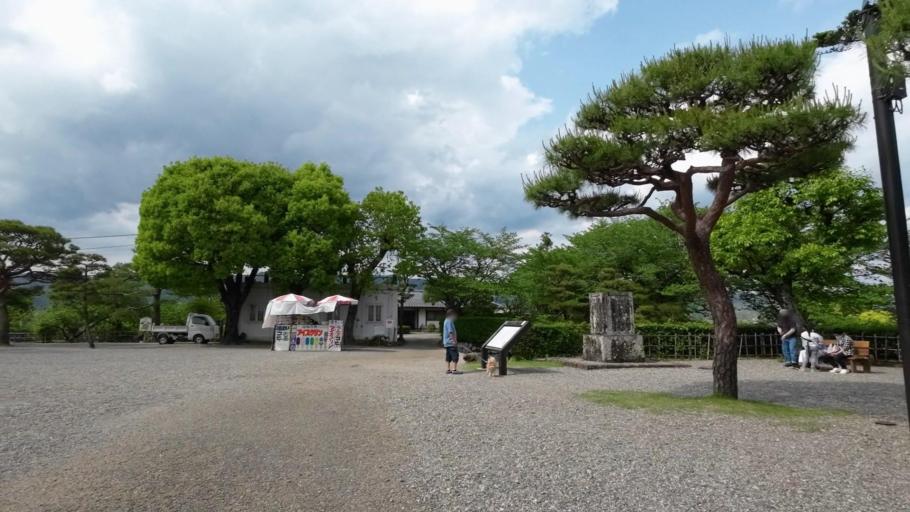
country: JP
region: Kochi
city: Kochi-shi
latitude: 33.5612
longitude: 133.5312
